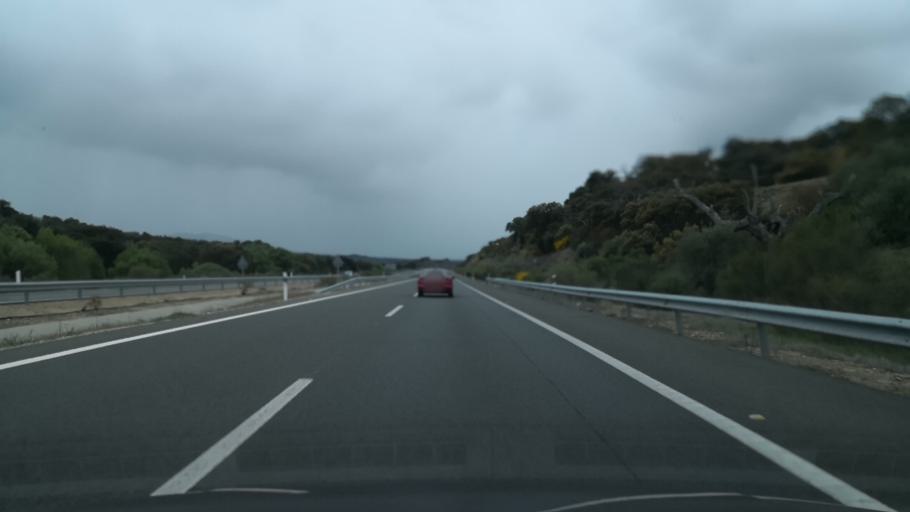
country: ES
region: Extremadura
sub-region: Provincia de Caceres
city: Oliva de Plasencia
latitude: 40.0769
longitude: -6.0922
